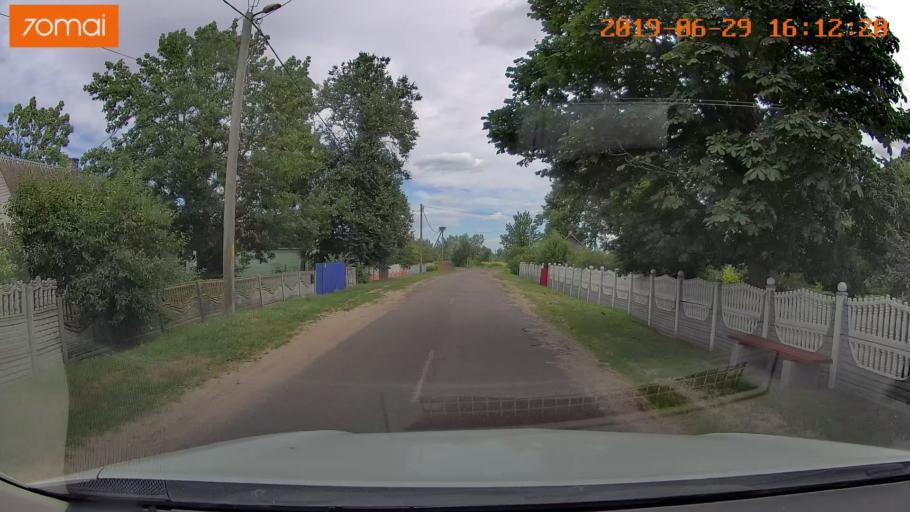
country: BY
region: Brest
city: Luninyets
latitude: 52.2009
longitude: 27.0142
